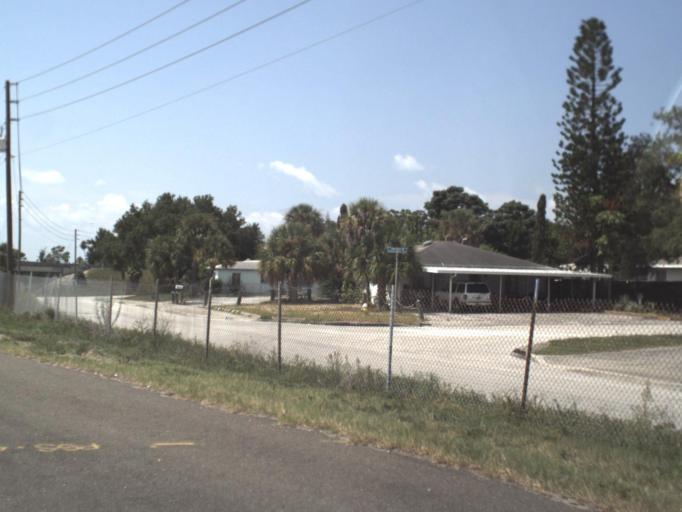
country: US
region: Florida
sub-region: Pinellas County
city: Bay Pines
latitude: 27.8162
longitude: -82.7871
